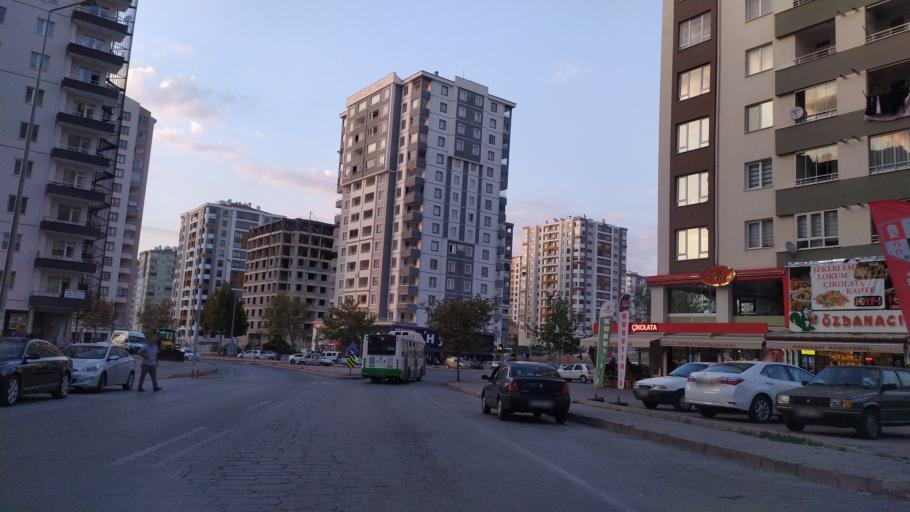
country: TR
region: Kayseri
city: Talas
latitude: 38.7078
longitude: 35.5628
